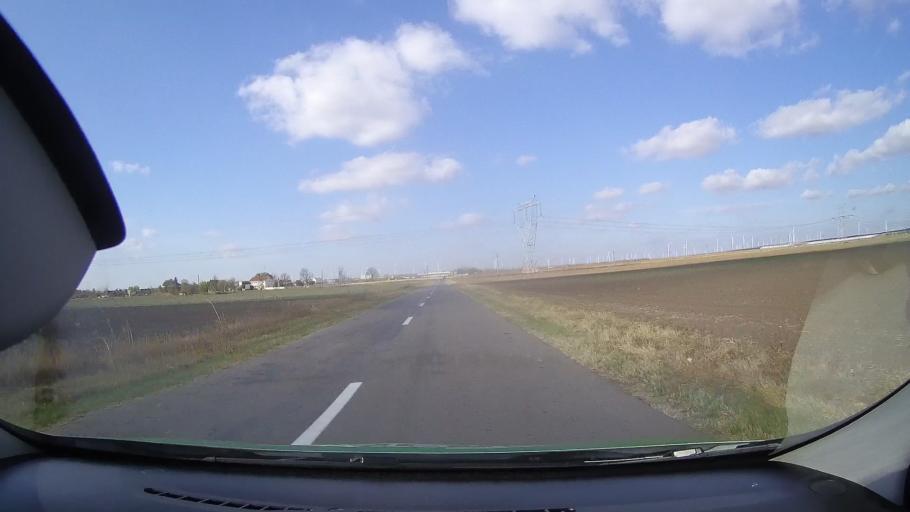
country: RO
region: Constanta
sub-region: Comuna Cogealac
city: Tariverde
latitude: 44.5575
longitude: 28.6143
